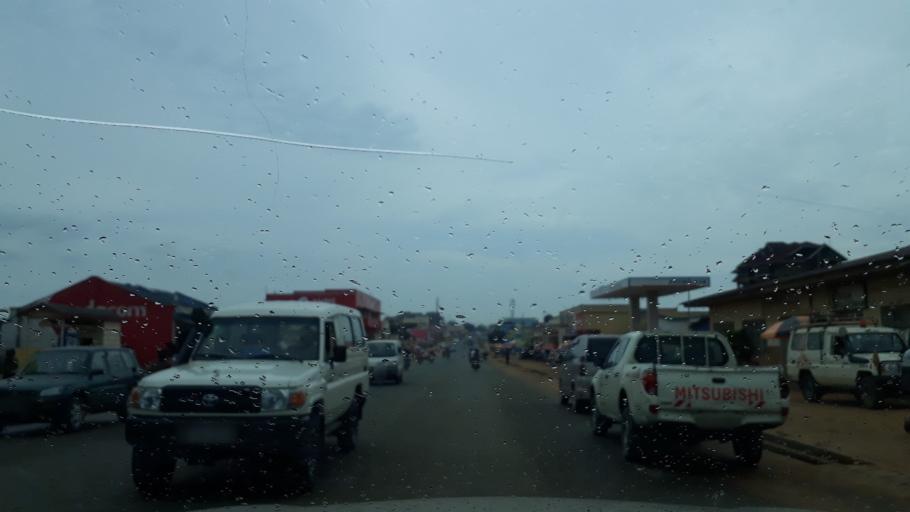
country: CD
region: Eastern Province
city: Bunia
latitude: 1.5603
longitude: 30.2480
